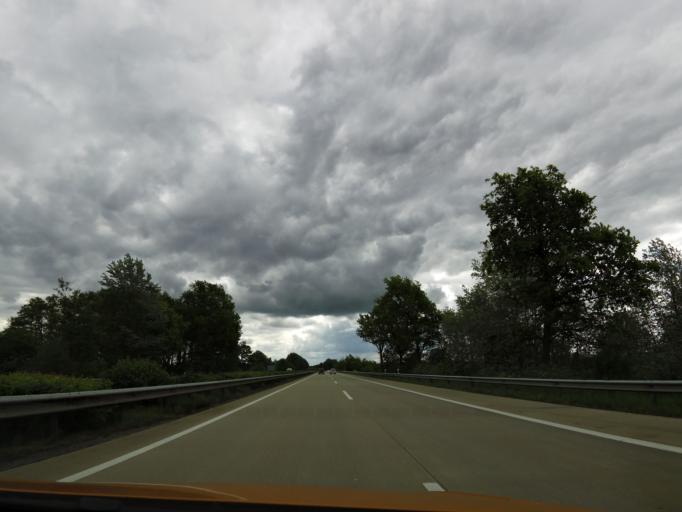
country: DE
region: Lower Saxony
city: Walsrode
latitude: 52.8184
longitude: 9.6162
